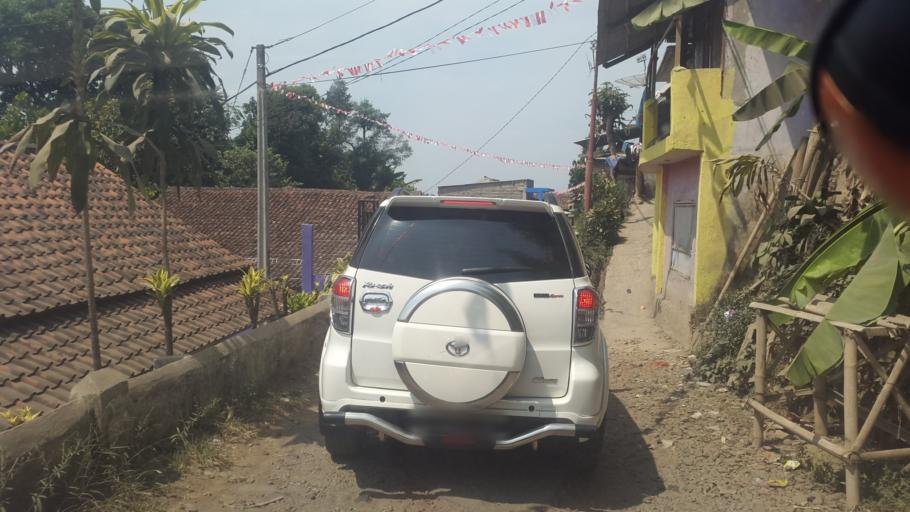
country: ID
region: West Java
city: Cicurug
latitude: -6.7726
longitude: 106.7388
